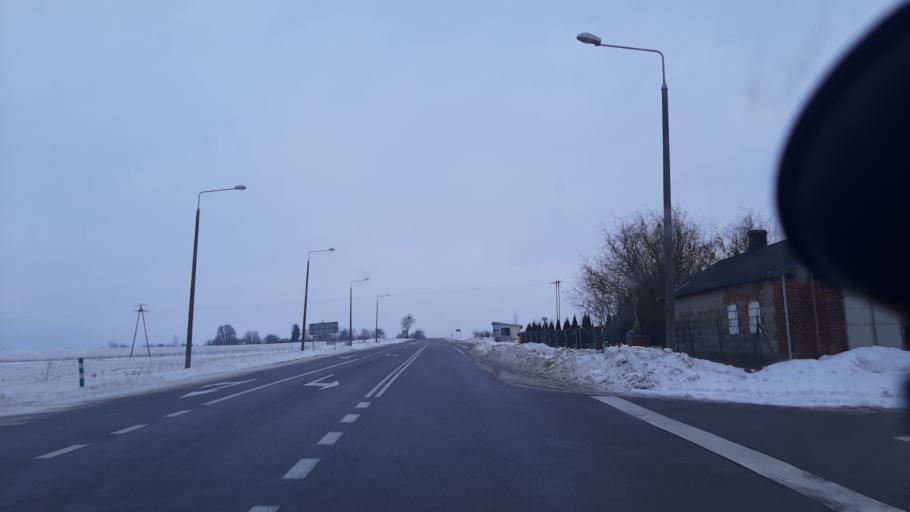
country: PL
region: Lublin Voivodeship
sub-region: Powiat pulawski
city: Markuszow
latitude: 51.3692
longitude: 22.2811
